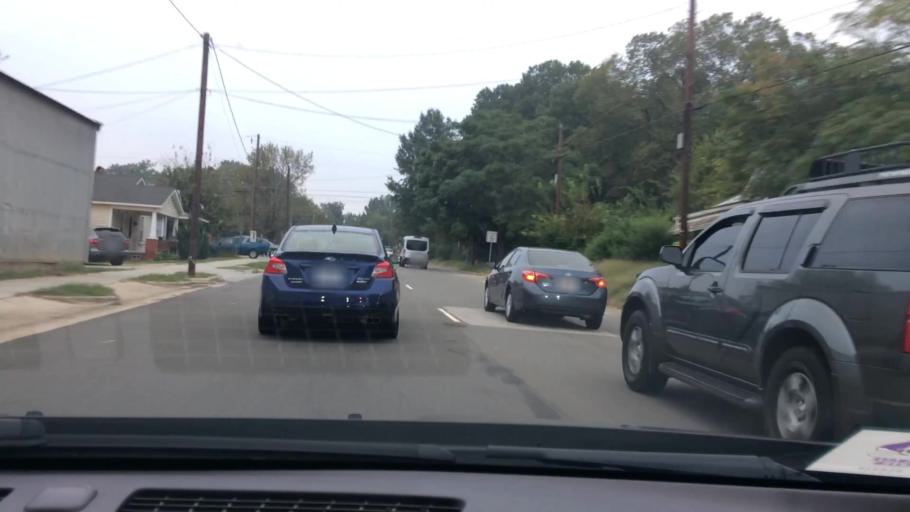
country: US
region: North Carolina
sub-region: Wake County
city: Raleigh
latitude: 35.7639
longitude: -78.6357
